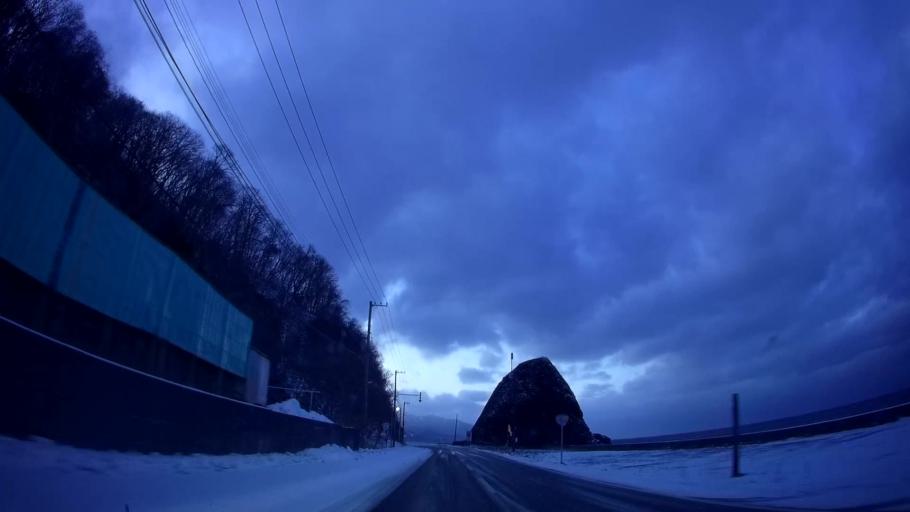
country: JP
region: Hokkaido
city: Hakodate
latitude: 41.8928
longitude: 141.0472
